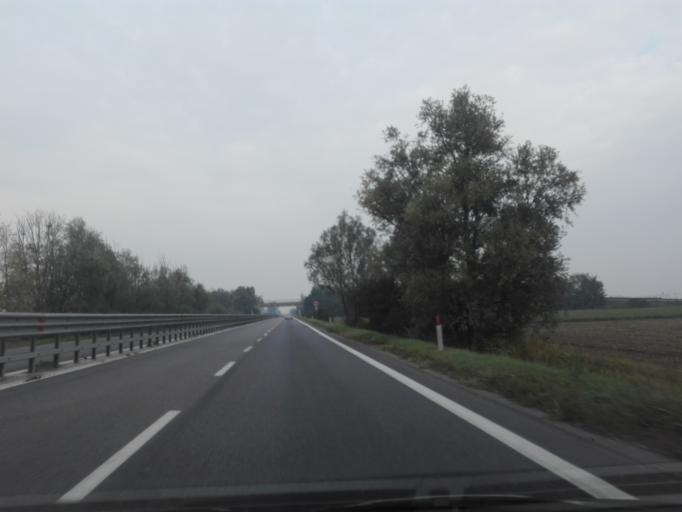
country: IT
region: Veneto
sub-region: Provincia di Rovigo
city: San Bellino
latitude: 45.0286
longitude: 11.5731
